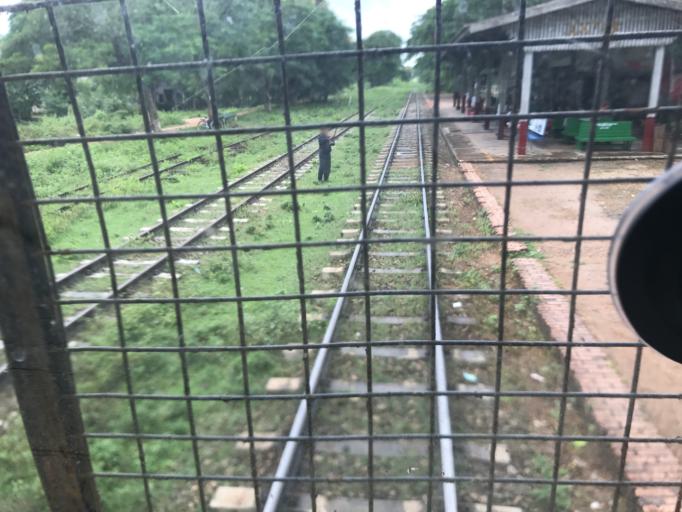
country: MM
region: Bago
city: Paungde
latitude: 18.6475
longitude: 95.4144
